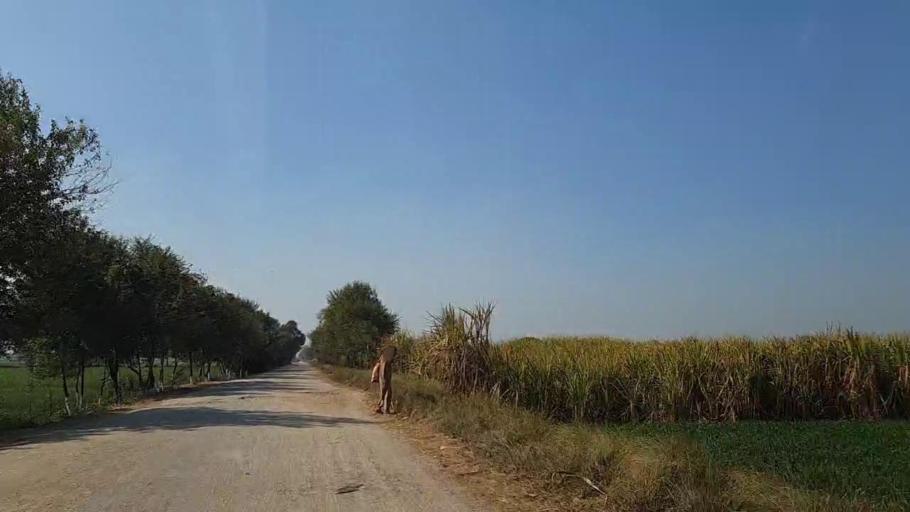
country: PK
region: Sindh
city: Sakrand
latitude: 26.2906
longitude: 68.0963
